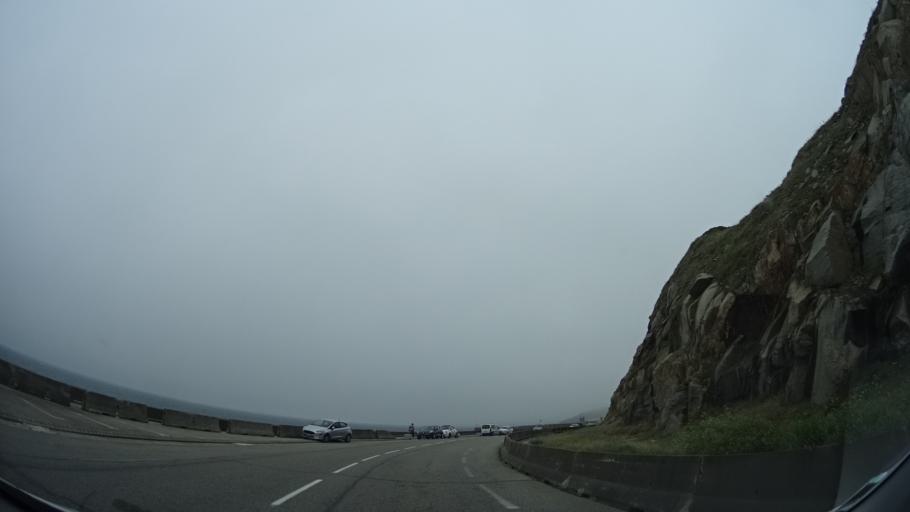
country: FR
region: Lower Normandy
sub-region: Departement de la Manche
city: Flamanville
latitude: 49.5477
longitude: -1.8692
